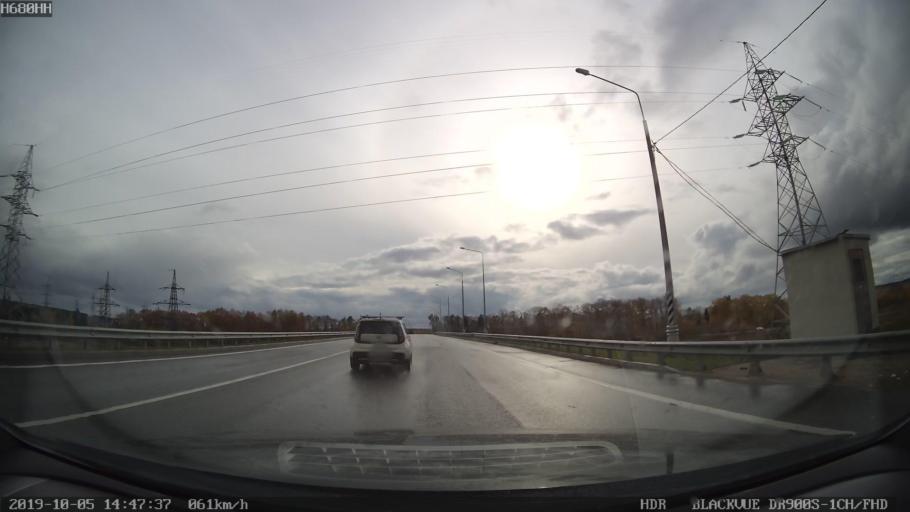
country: RU
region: Moskovskaya
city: Solnechnogorsk
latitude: 56.2198
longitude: 36.9074
